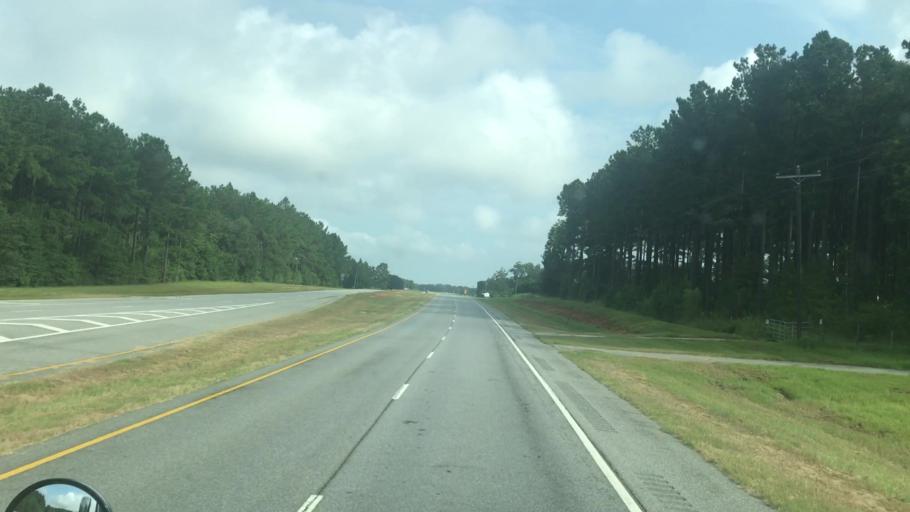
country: US
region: Georgia
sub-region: Miller County
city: Colquitt
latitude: 31.2284
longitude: -84.7816
